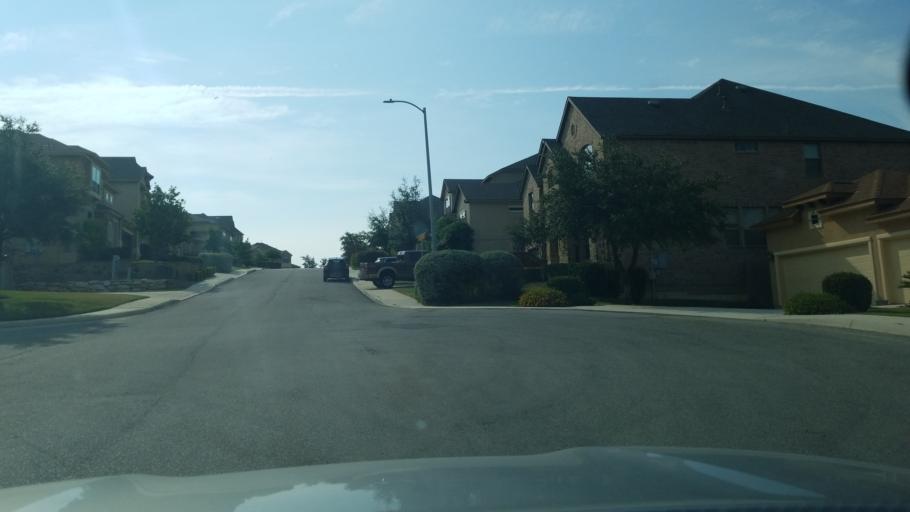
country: US
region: Texas
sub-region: Bexar County
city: Scenic Oaks
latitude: 29.7147
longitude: -98.6562
